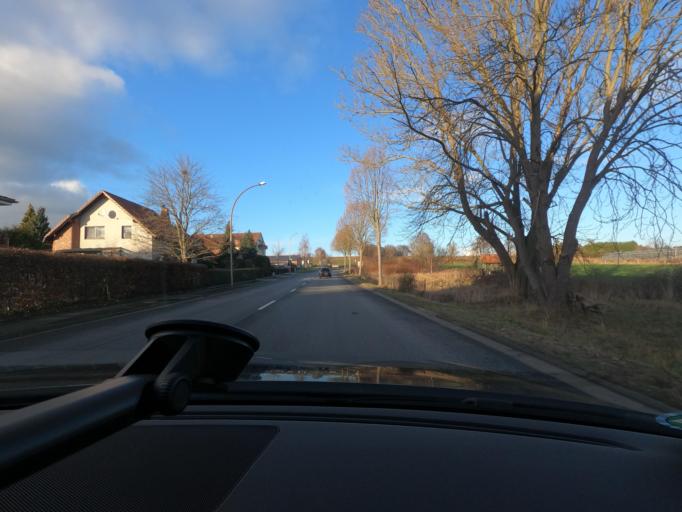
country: DE
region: Lower Saxony
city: Duderstadt
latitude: 51.5187
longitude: 10.2607
